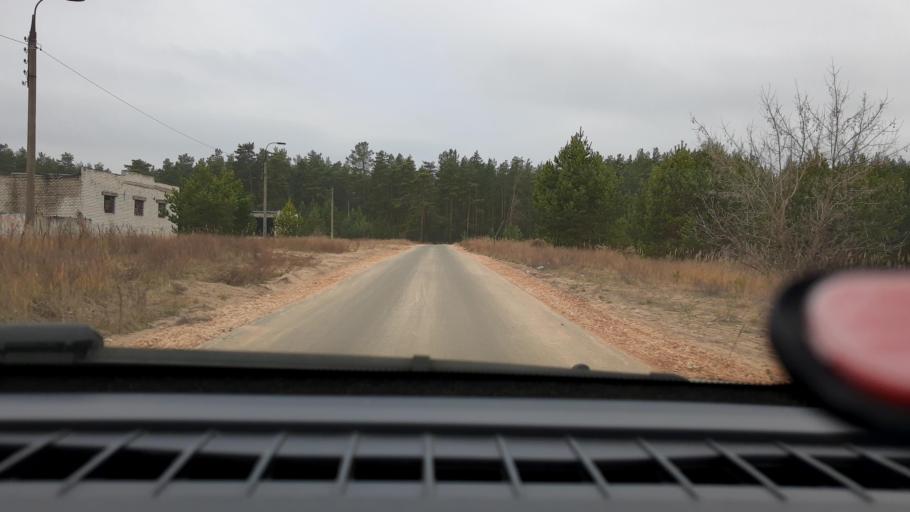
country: RU
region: Nizjnij Novgorod
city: Lukino
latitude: 56.3923
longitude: 43.7165
